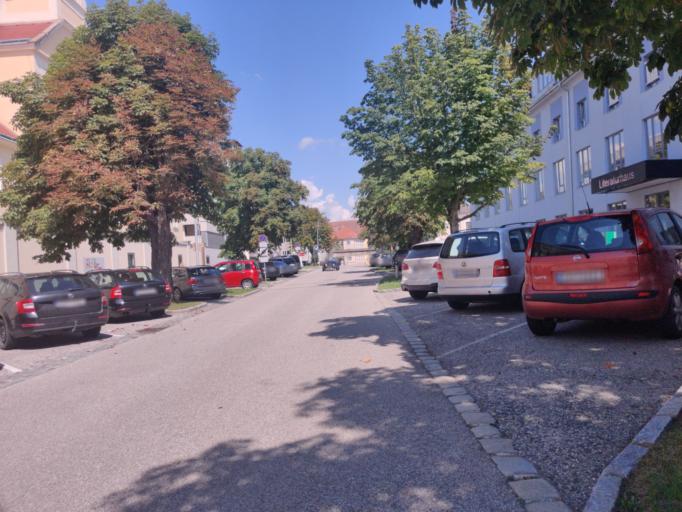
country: AT
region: Lower Austria
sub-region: Politischer Bezirk Krems
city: Weinzierl bei Krems
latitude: 48.4051
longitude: 15.5882
